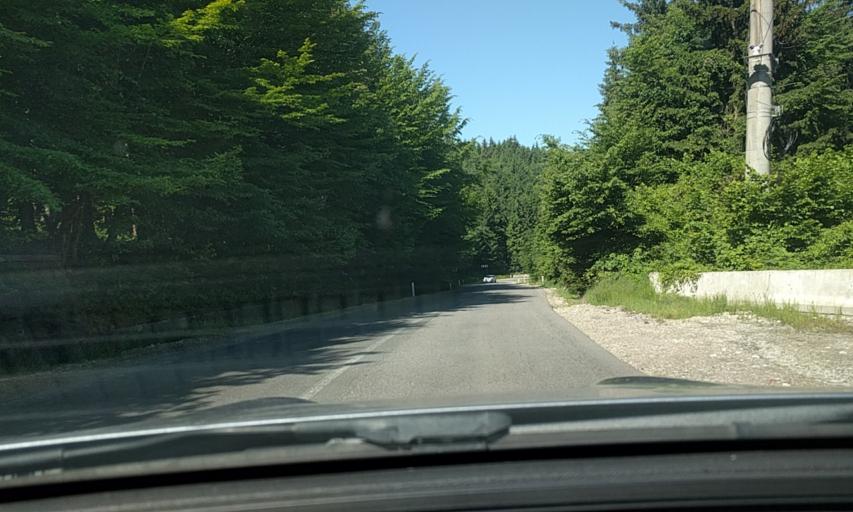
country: RO
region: Bistrita-Nasaud
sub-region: Comuna Dumitra
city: Dumitra
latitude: 47.1899
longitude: 24.4814
